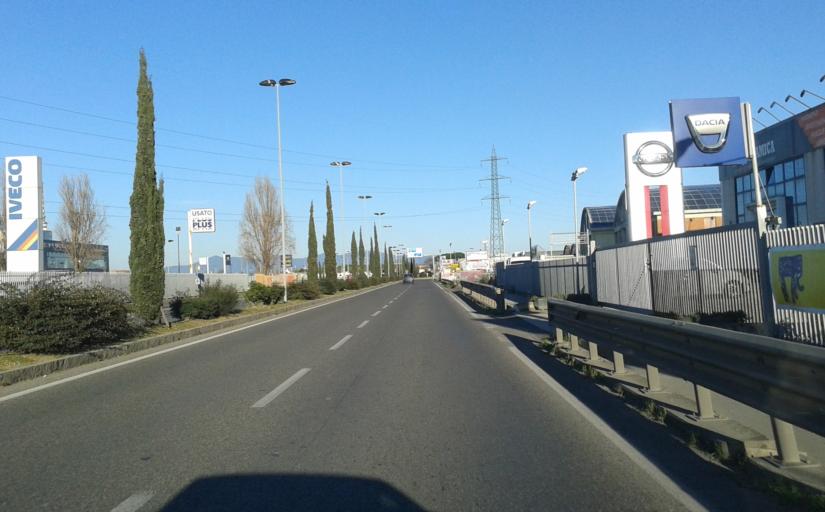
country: IT
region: Tuscany
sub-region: Provincia di Livorno
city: Livorno
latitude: 43.5754
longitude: 10.3366
